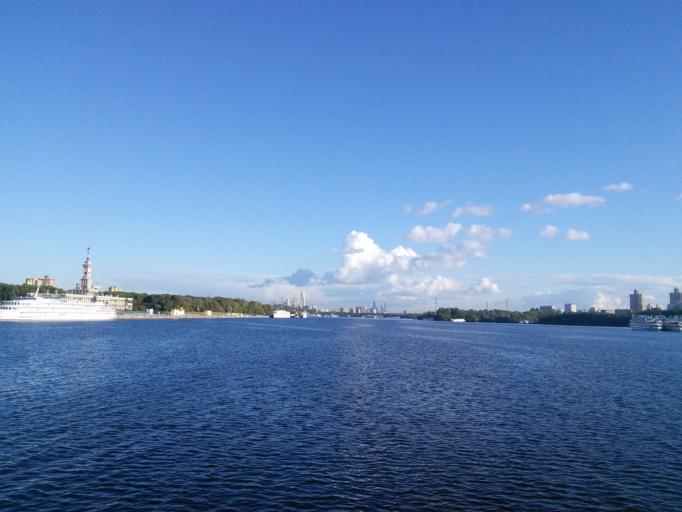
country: RU
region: Moskovskaya
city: Levoberezhnyy
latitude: 55.8539
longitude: 37.4606
